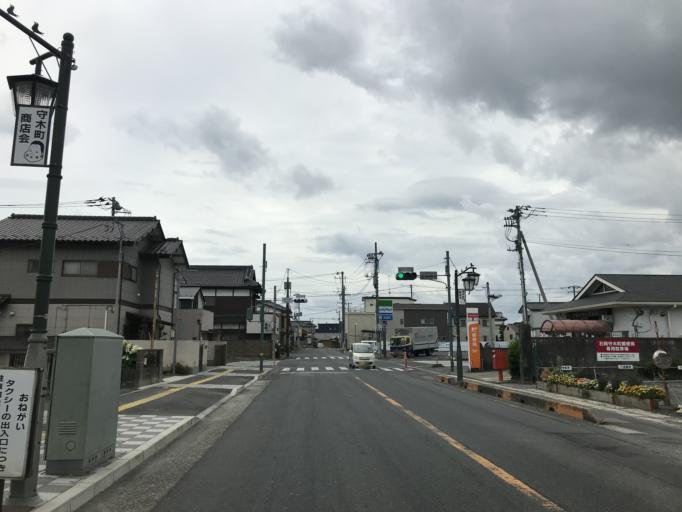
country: JP
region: Ibaraki
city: Ishioka
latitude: 36.1867
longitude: 140.2741
